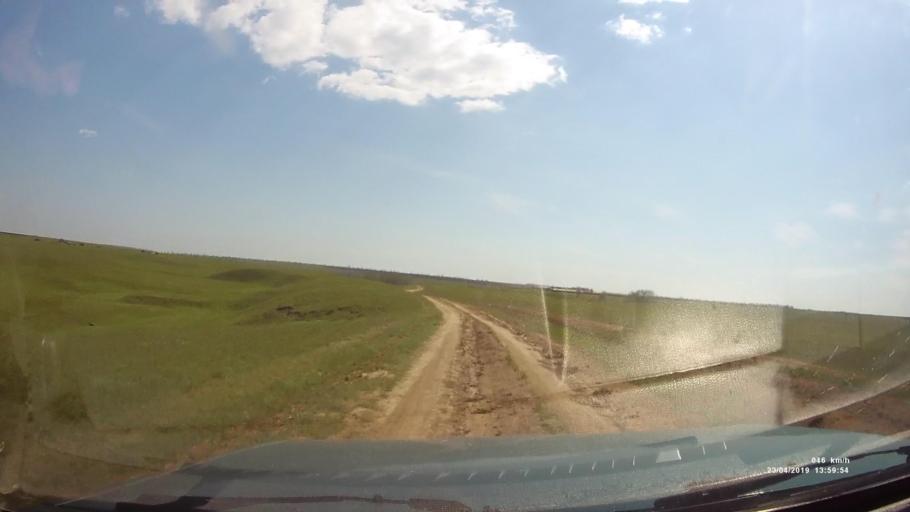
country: RU
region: Rostov
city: Remontnoye
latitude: 46.5632
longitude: 42.9468
